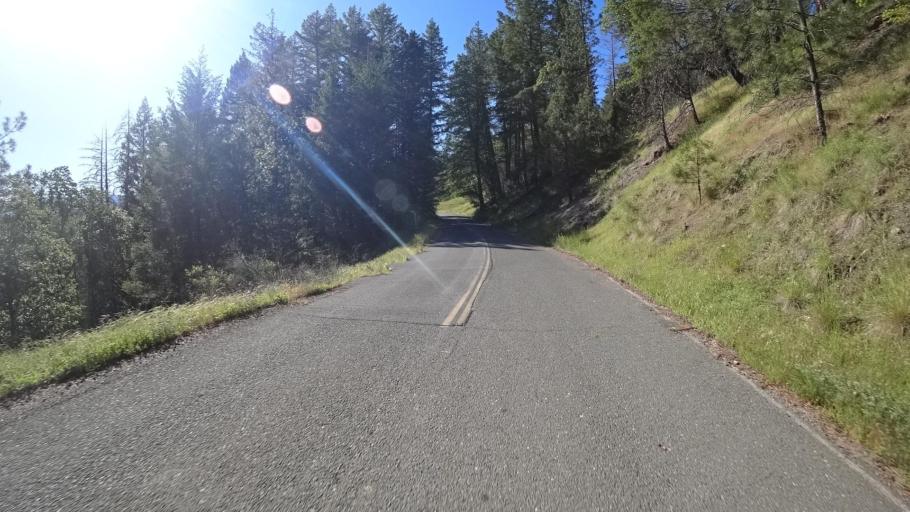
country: US
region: California
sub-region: Lake County
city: Upper Lake
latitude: 39.4071
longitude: -122.9742
